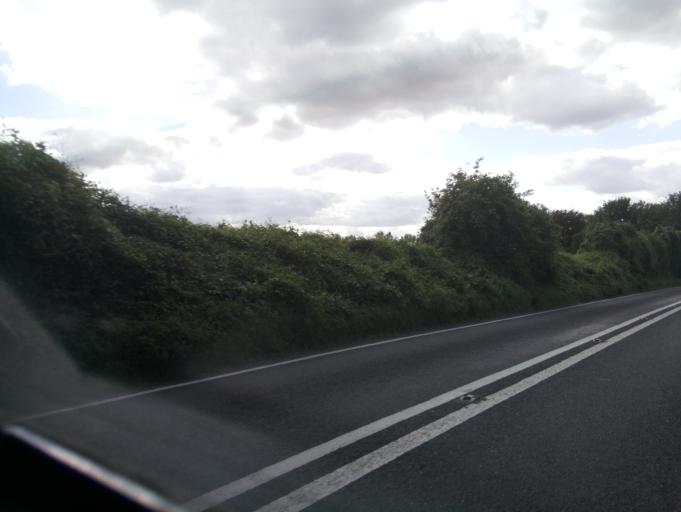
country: GB
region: England
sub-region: Hampshire
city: Winchester
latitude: 51.0987
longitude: -1.3932
